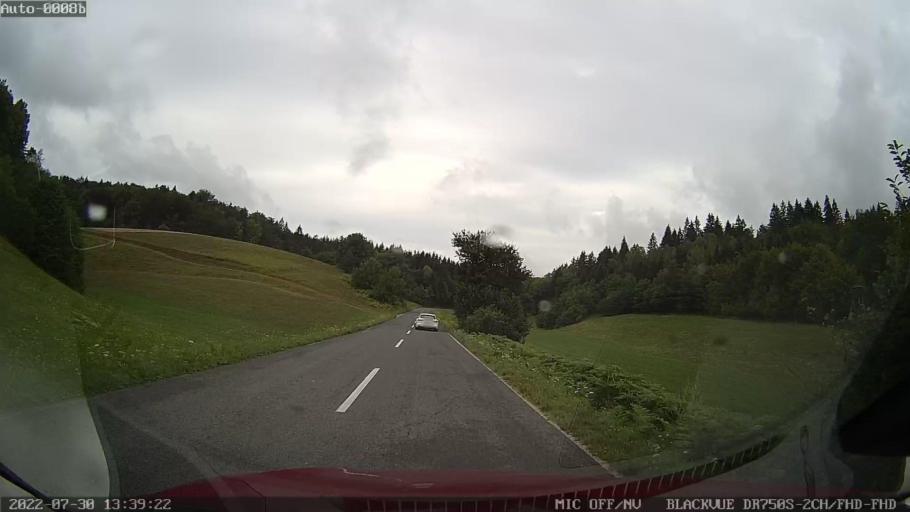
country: SI
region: Zuzemberk
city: Zuzemberk
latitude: 45.8930
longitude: 14.9073
